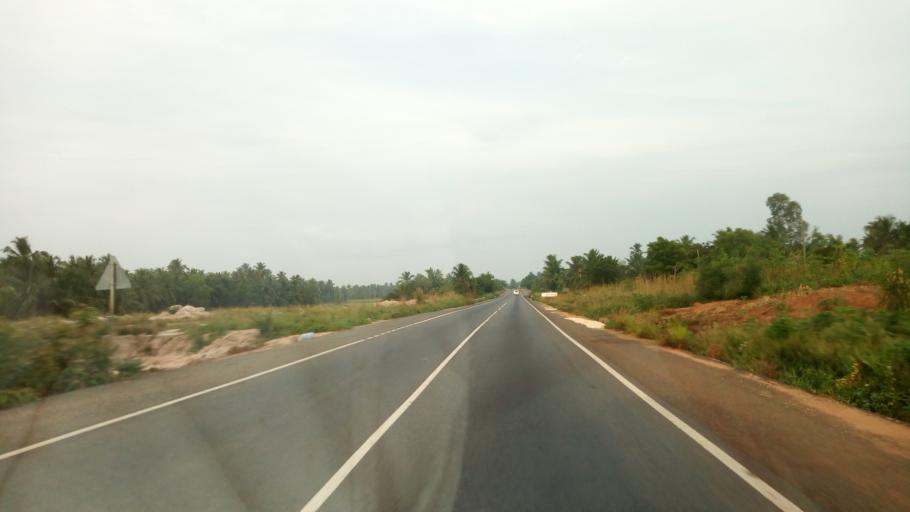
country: TG
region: Maritime
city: Lome
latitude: 6.0974
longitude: 1.0900
